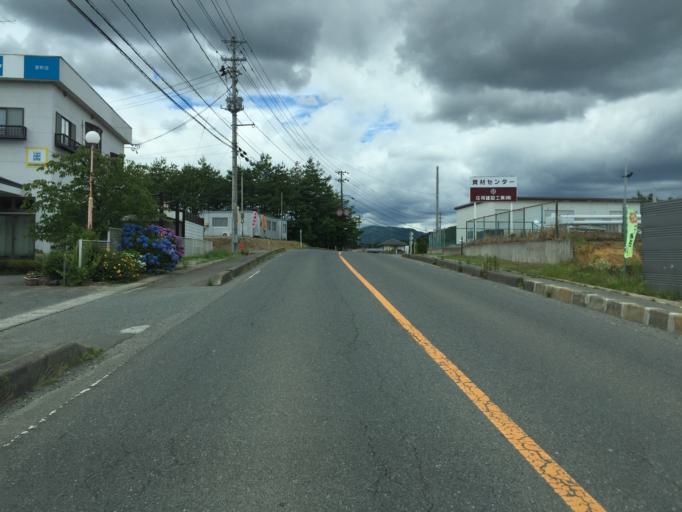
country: JP
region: Fukushima
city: Namie
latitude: 37.6217
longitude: 140.9805
